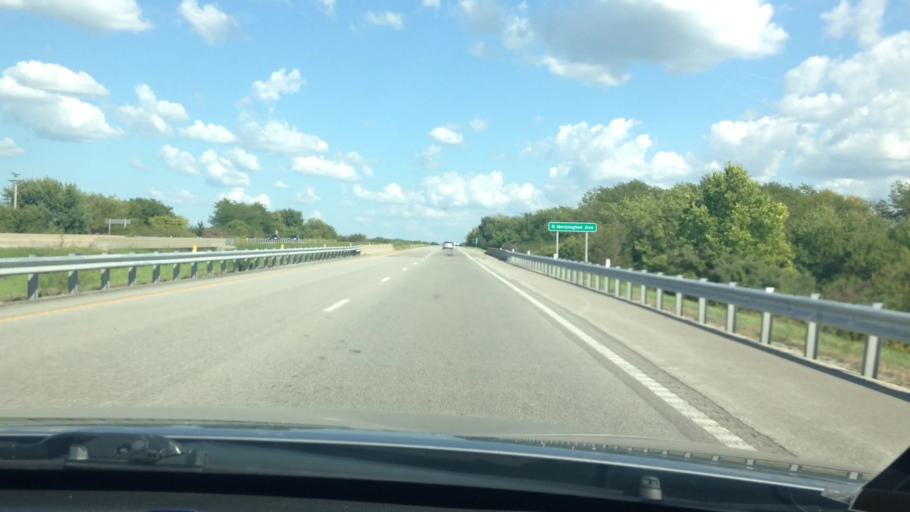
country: US
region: Missouri
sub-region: Clay County
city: Smithville
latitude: 39.3109
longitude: -94.5350
